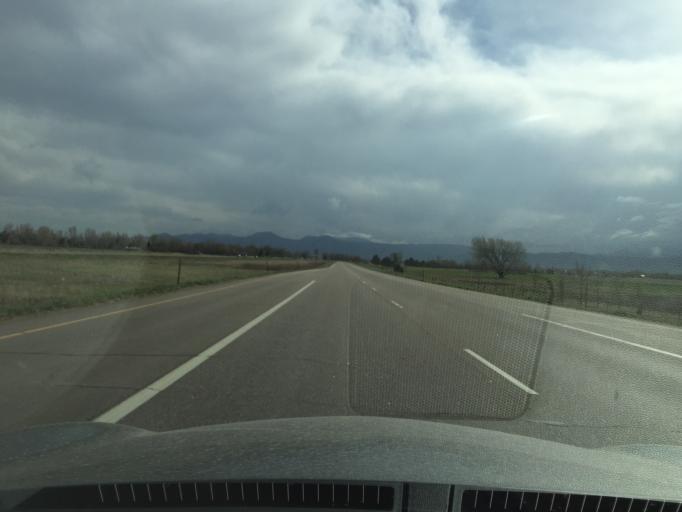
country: US
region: Colorado
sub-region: Boulder County
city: Niwot
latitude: 40.1159
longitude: -105.1616
